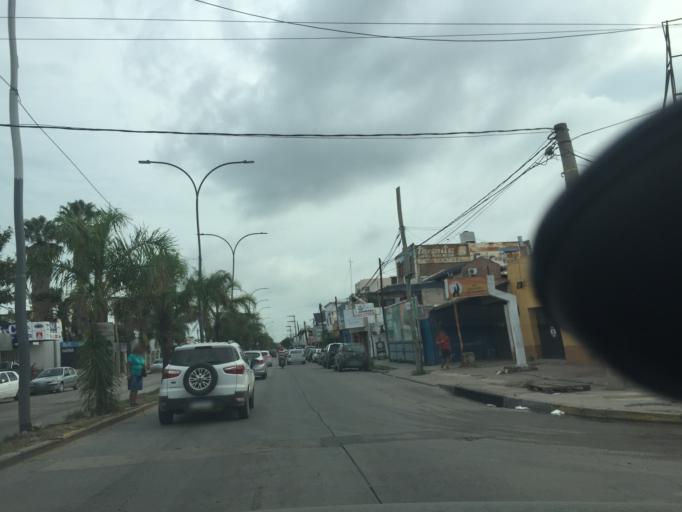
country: AR
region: Cordoba
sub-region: Departamento de Capital
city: Cordoba
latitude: -31.4451
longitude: -64.1982
